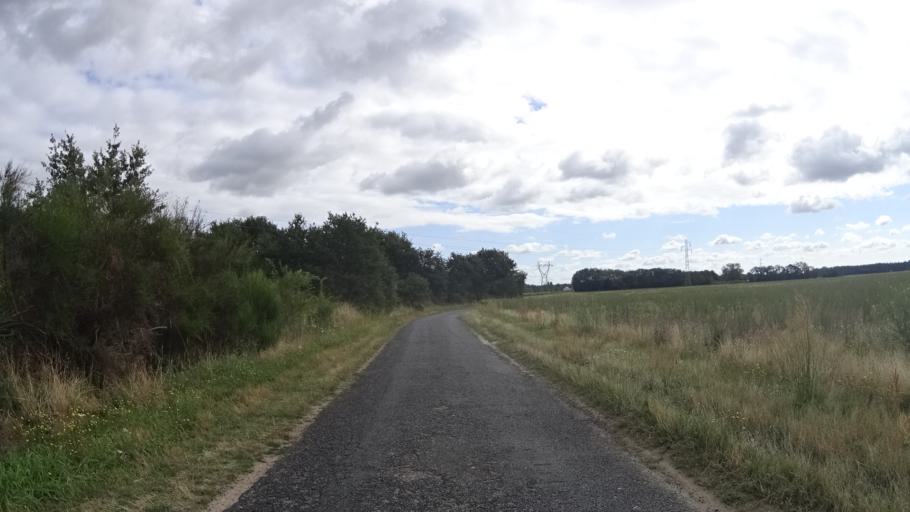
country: FR
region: Centre
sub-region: Departement d'Indre-et-Loire
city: Avoine
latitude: 47.2264
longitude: 0.1788
